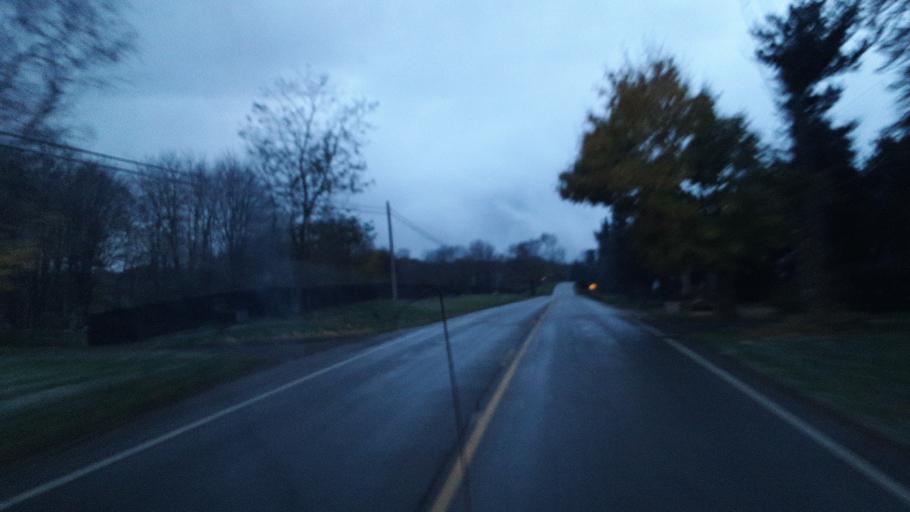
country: US
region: Ohio
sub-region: Portage County
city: Mantua
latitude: 41.3403
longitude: -81.2223
